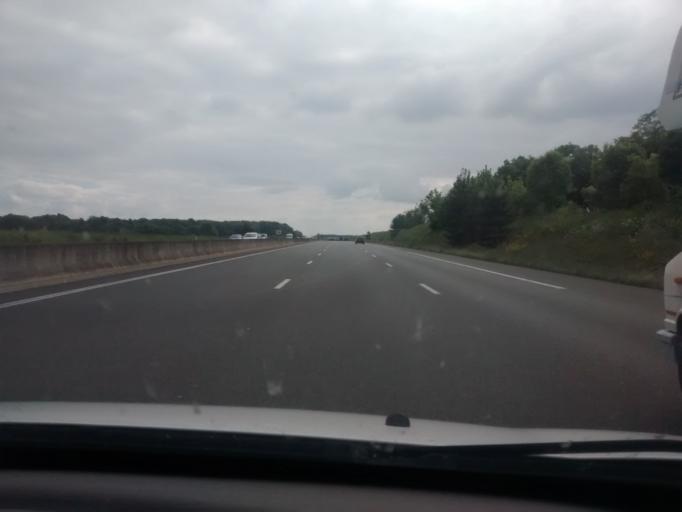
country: FR
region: Centre
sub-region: Departement d'Eure-et-Loir
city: Brou
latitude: 48.2619
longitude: 1.1405
